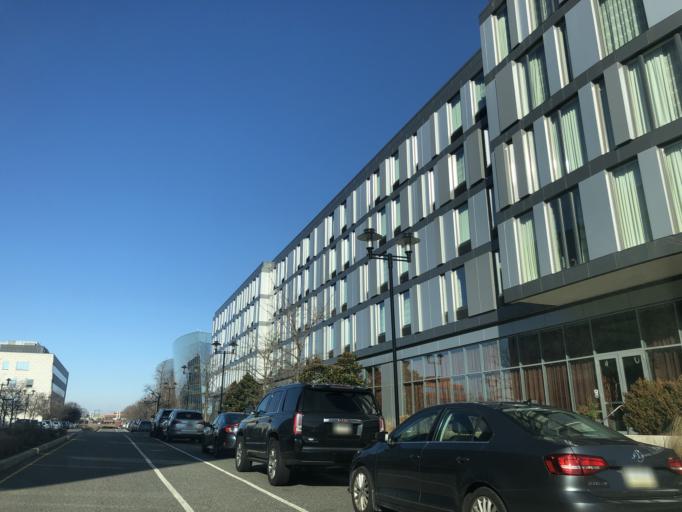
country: US
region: New Jersey
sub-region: Gloucester County
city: National Park
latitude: 39.8953
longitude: -75.1723
